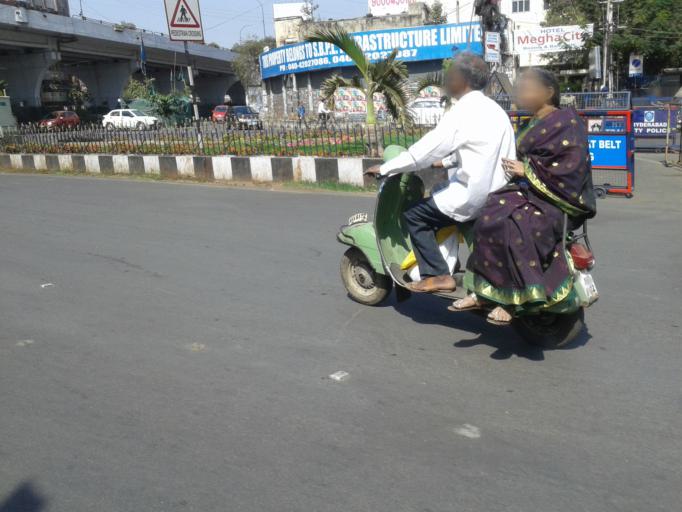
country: IN
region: Telangana
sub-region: Hyderabad
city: Hyderabad
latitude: 17.4009
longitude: 78.4759
